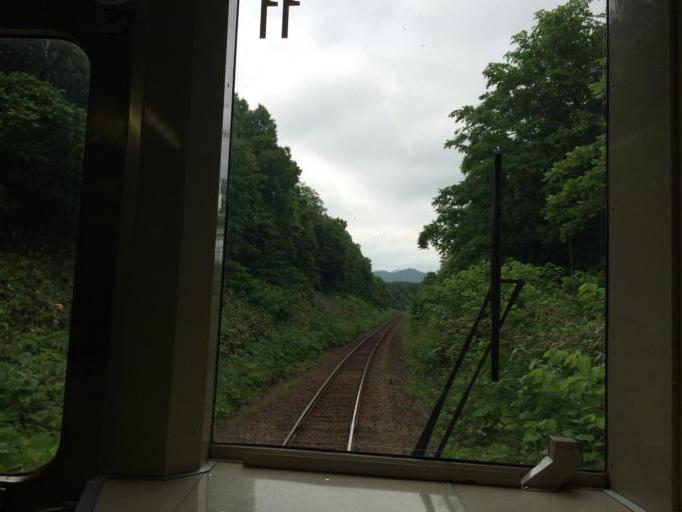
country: JP
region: Hokkaido
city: Yoichi
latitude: 43.0660
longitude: 140.7027
